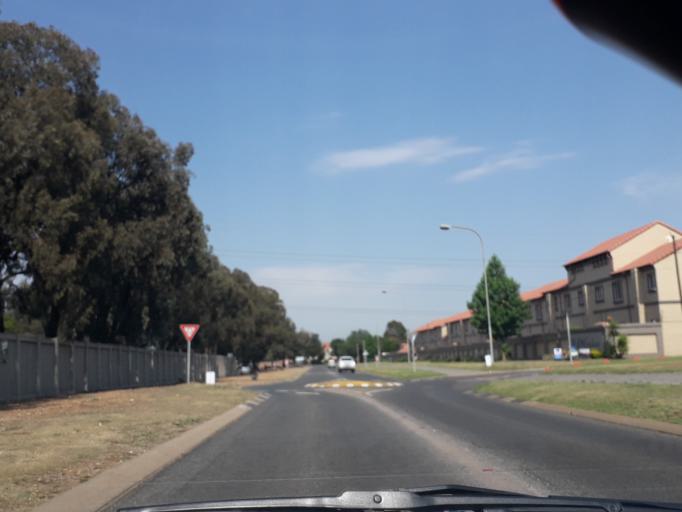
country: ZA
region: Gauteng
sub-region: City of Johannesburg Metropolitan Municipality
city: Modderfontein
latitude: -26.1374
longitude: 28.1853
